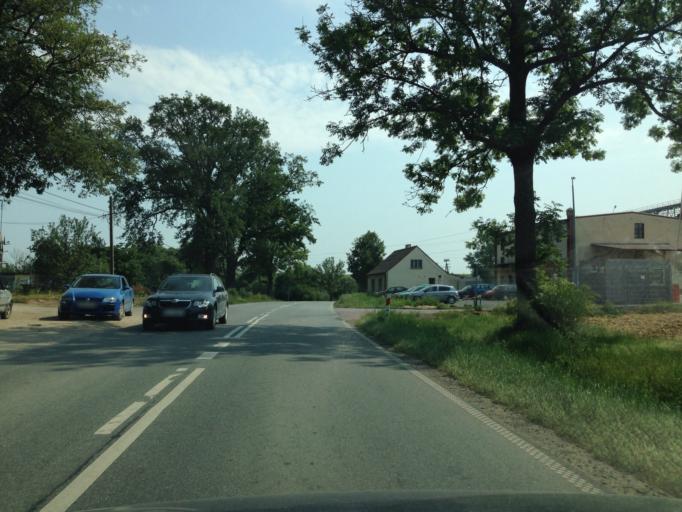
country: PL
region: Kujawsko-Pomorskie
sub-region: Powiat golubsko-dobrzynski
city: Radomin
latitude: 53.0956
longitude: 19.1542
